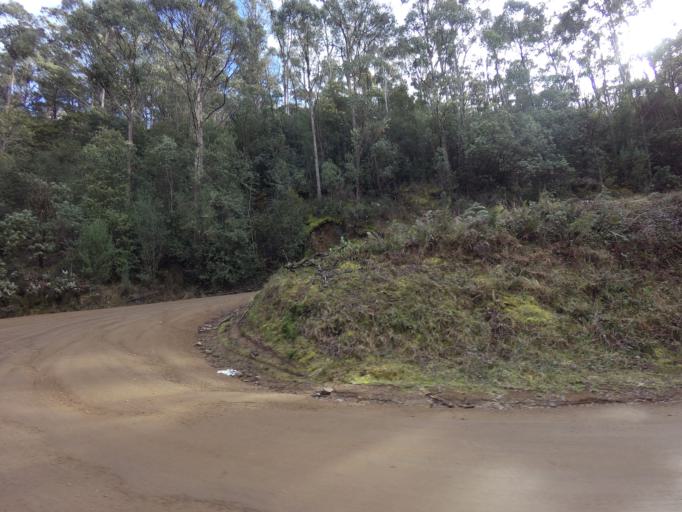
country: AU
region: Tasmania
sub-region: Derwent Valley
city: New Norfolk
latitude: -42.7910
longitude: 146.9351
